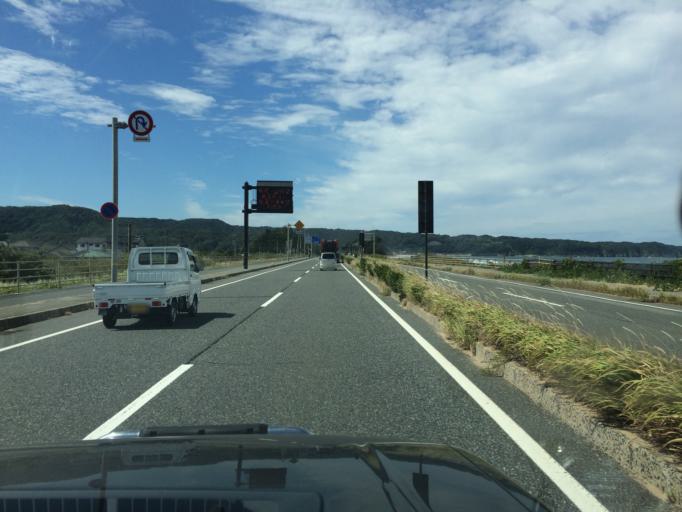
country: JP
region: Tottori
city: Tottori
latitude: 35.5179
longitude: 134.0486
